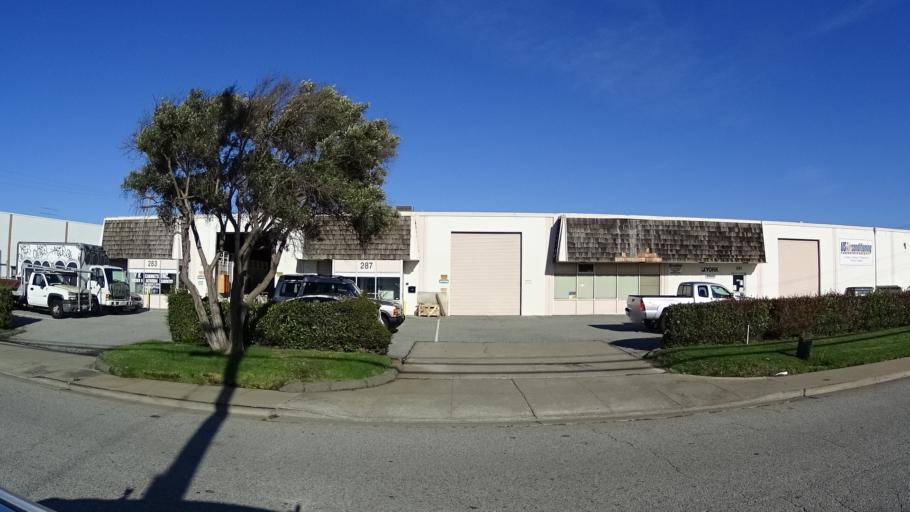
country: US
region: California
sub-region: San Mateo County
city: South San Francisco
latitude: 37.6477
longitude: -122.4001
